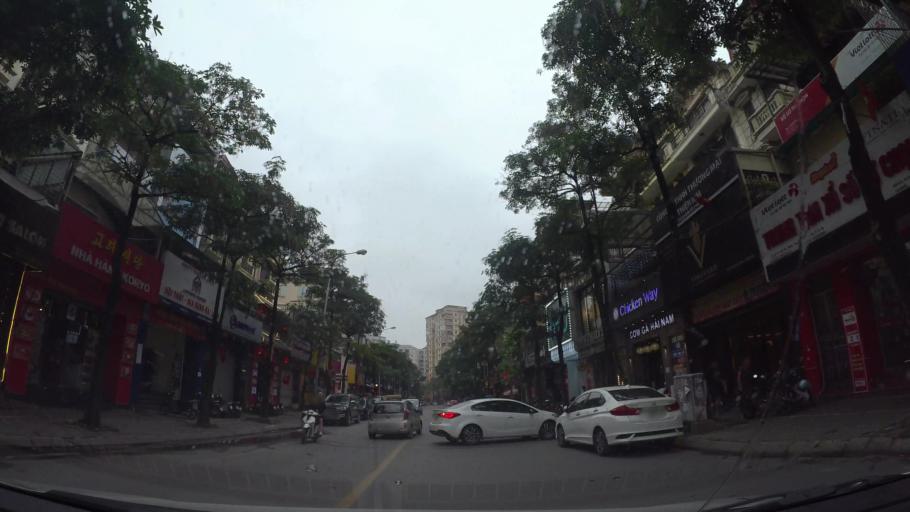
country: VN
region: Ha Noi
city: Cau Giay
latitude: 21.0159
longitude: 105.8005
